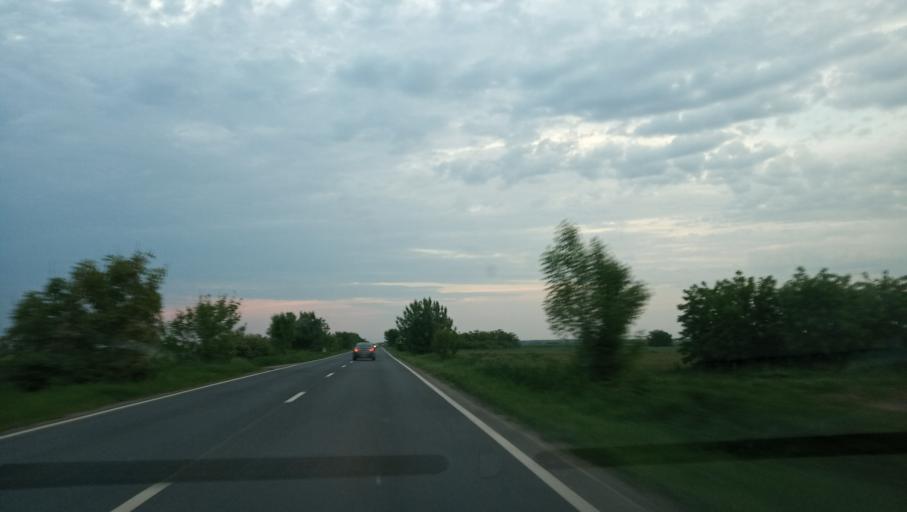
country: RO
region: Timis
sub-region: Comuna Padureni
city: Padureni
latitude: 45.5813
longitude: 21.2019
